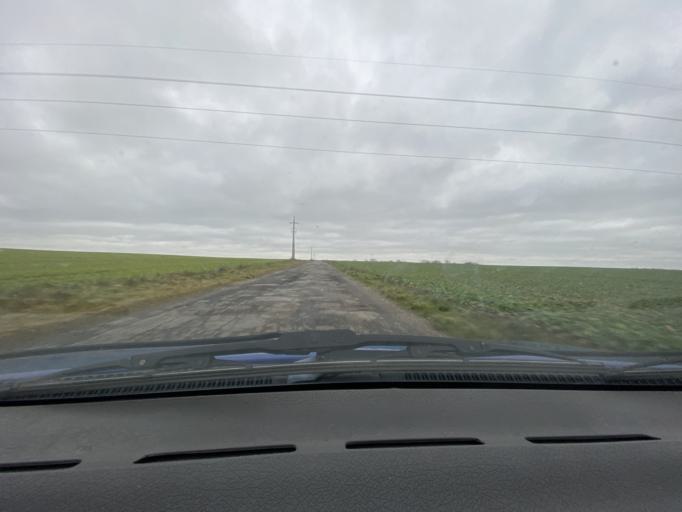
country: PL
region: West Pomeranian Voivodeship
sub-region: Powiat gryficki
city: Gryfice
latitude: 53.9546
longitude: 15.2591
